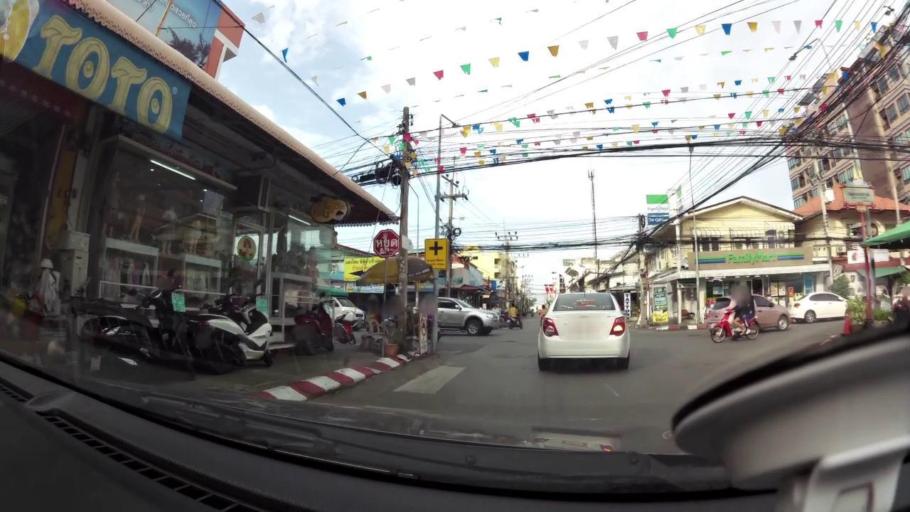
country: TH
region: Prachuap Khiri Khan
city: Hua Hin
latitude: 12.5734
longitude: 99.9567
